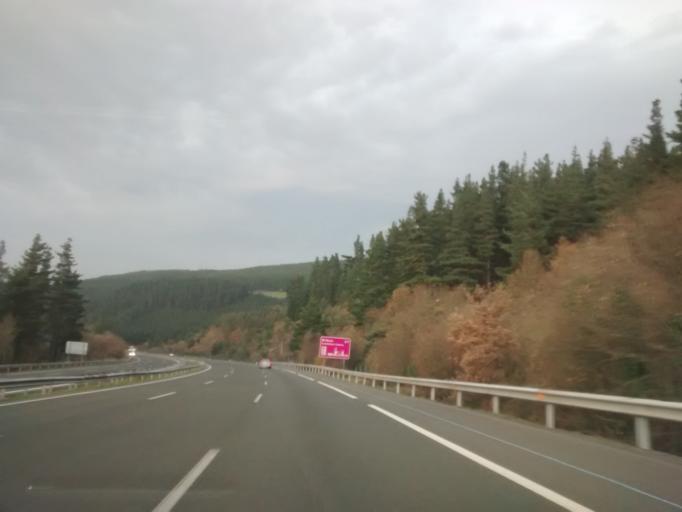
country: ES
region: Basque Country
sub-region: Provincia de Alava
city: Lezama
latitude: 43.0273
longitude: -2.9116
